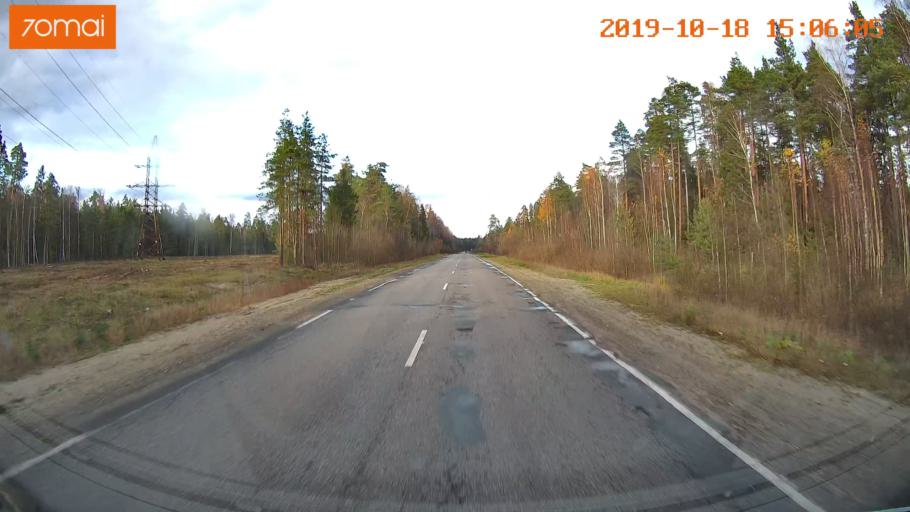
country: RU
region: Vladimir
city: Gus'-Khrustal'nyy
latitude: 55.5247
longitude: 40.5761
